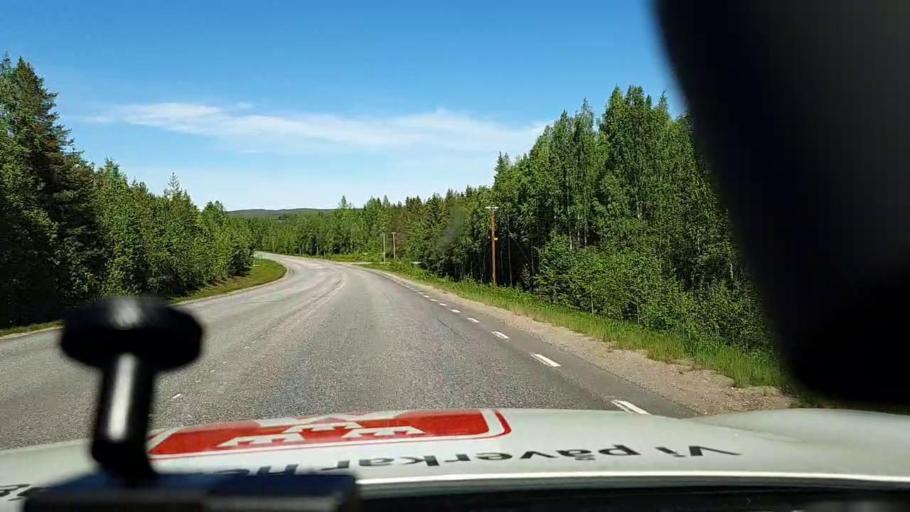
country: SE
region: Norrbotten
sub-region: Kalix Kommun
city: Toere
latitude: 66.1015
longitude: 22.7123
